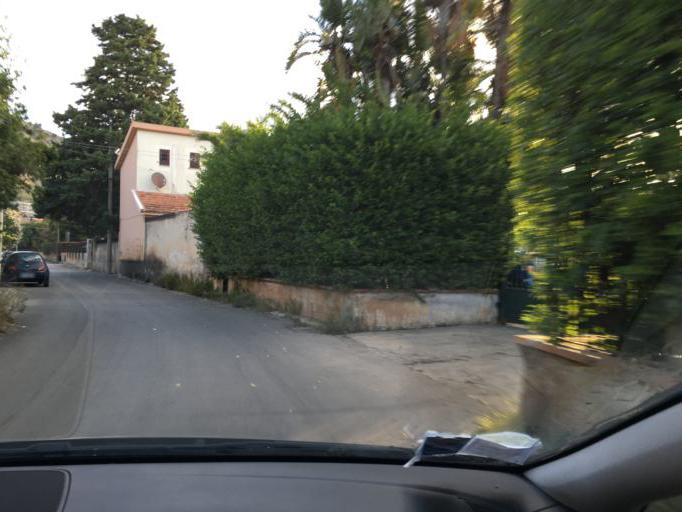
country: IT
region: Sicily
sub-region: Palermo
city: Palermo
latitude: 38.2025
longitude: 13.3211
